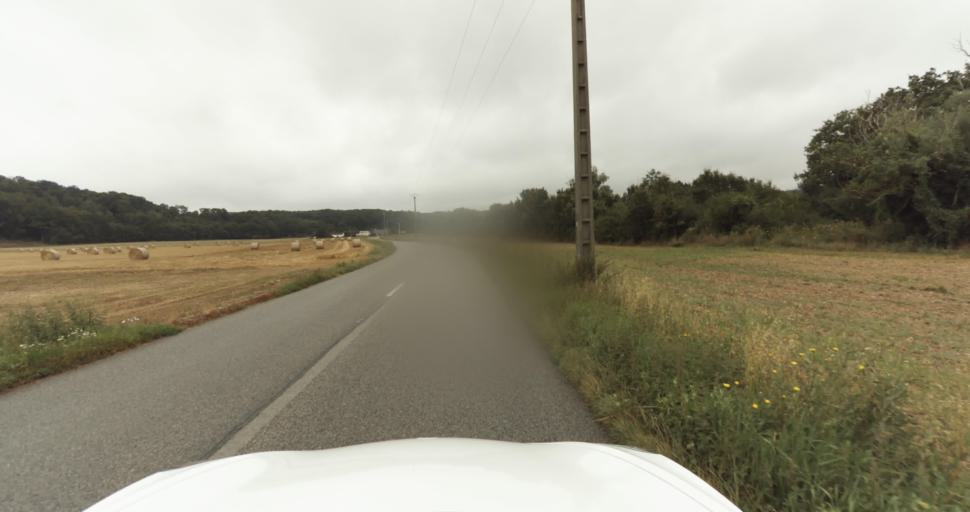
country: FR
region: Haute-Normandie
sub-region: Departement de l'Eure
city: Normanville
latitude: 49.0803
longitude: 1.1427
